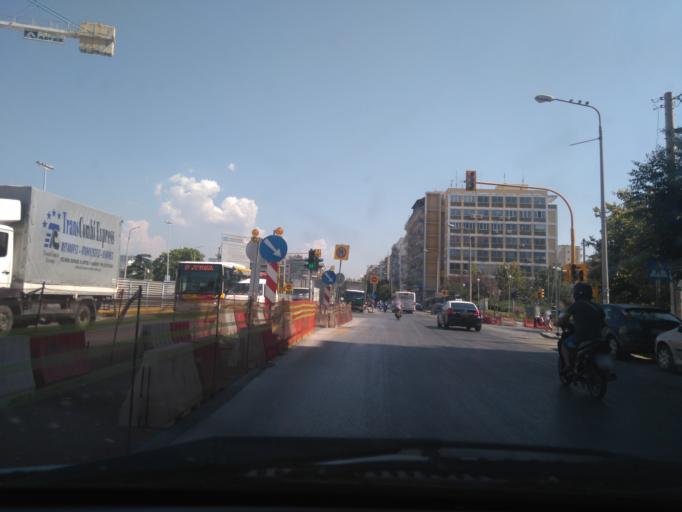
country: GR
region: Central Macedonia
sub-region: Nomos Thessalonikis
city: Thessaloniki
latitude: 40.6442
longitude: 22.9279
